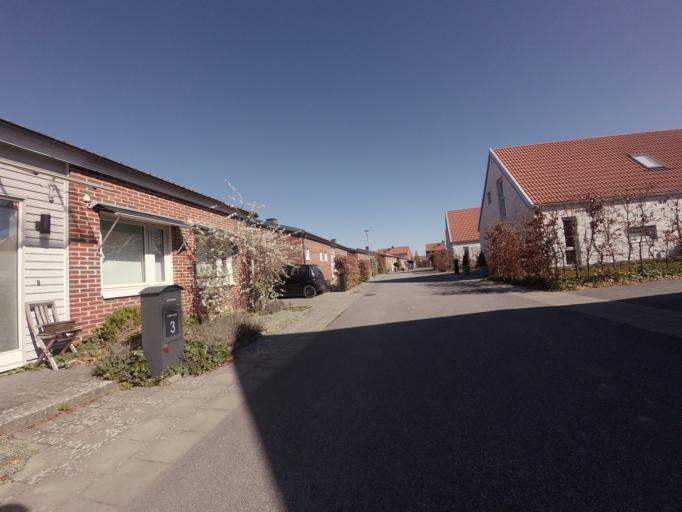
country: SE
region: Skane
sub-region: Lomma Kommun
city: Lomma
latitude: 55.6772
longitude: 13.0927
